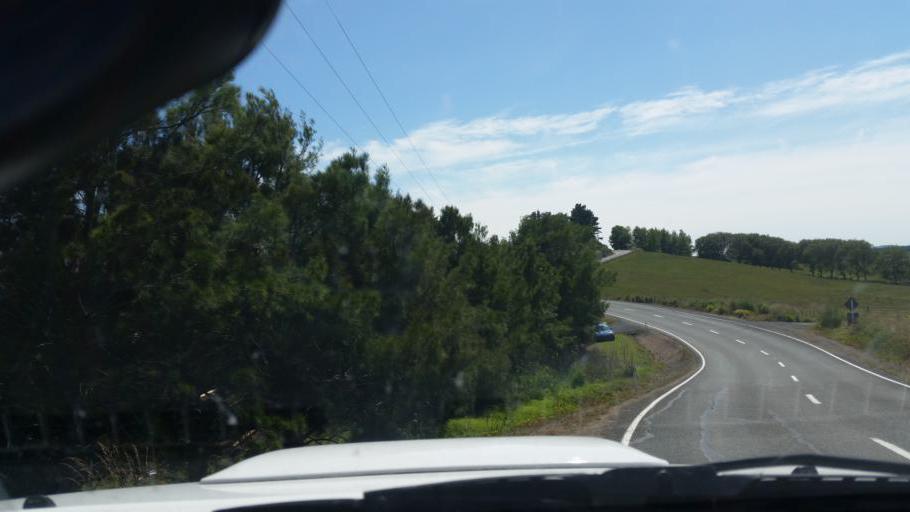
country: NZ
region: Auckland
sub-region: Auckland
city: Wellsford
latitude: -36.2250
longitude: 174.3736
